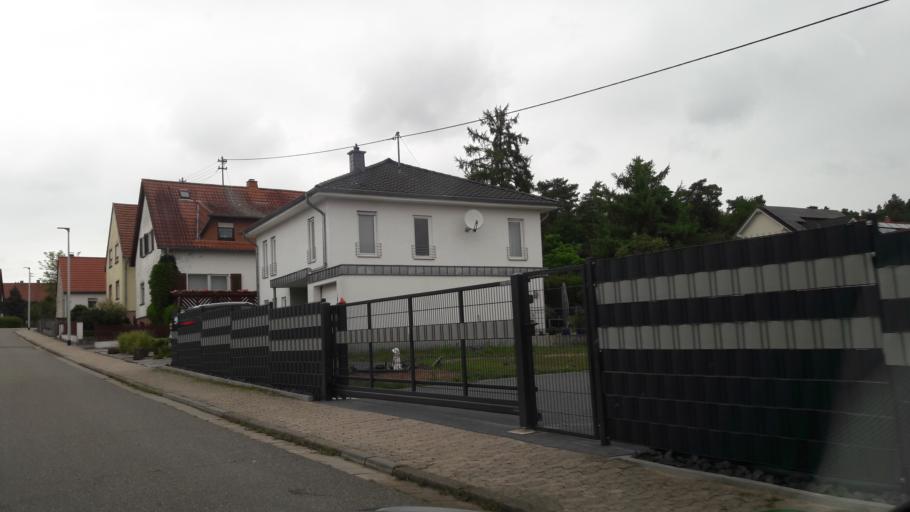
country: DE
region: Saarland
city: Bexbach
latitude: 49.3471
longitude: 7.2900
